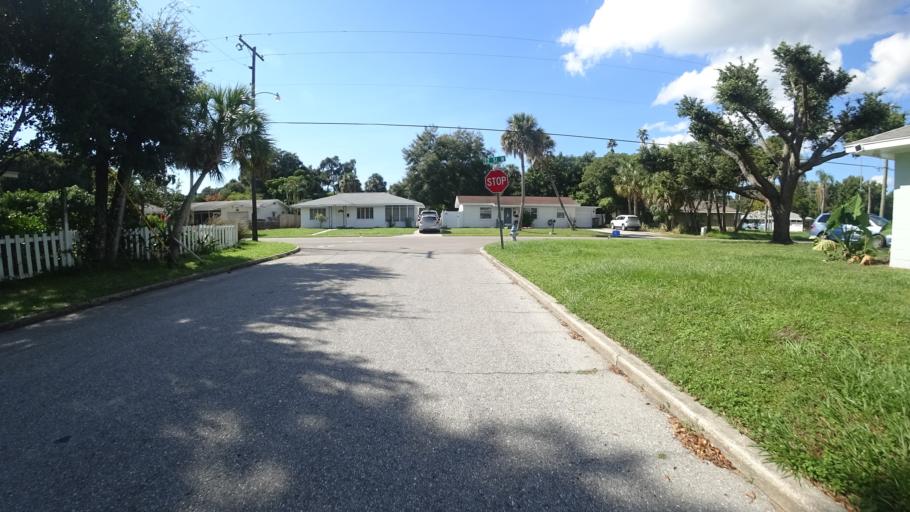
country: US
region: Florida
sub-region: Manatee County
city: Bradenton
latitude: 27.4837
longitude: -82.5833
